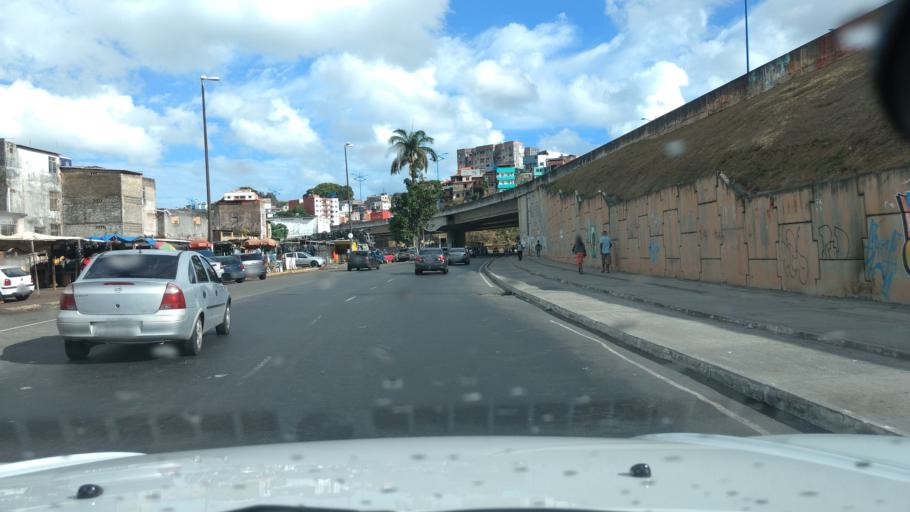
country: BR
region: Bahia
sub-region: Salvador
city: Salvador
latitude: -12.9648
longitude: -38.4925
